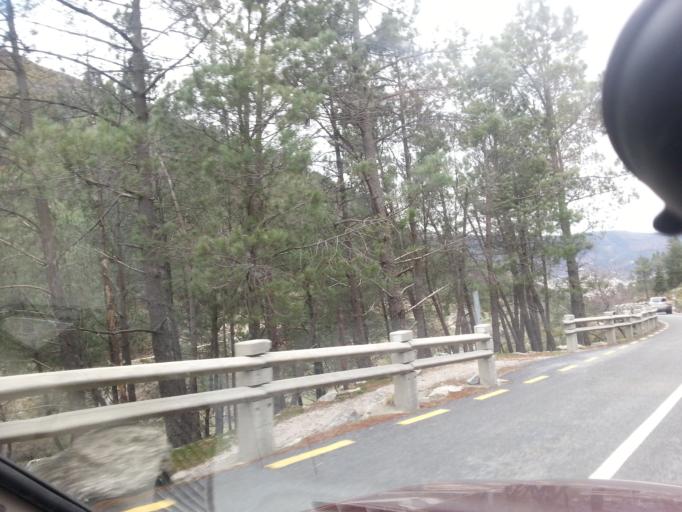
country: PT
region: Guarda
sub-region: Manteigas
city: Manteigas
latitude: 40.3641
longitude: -7.5533
